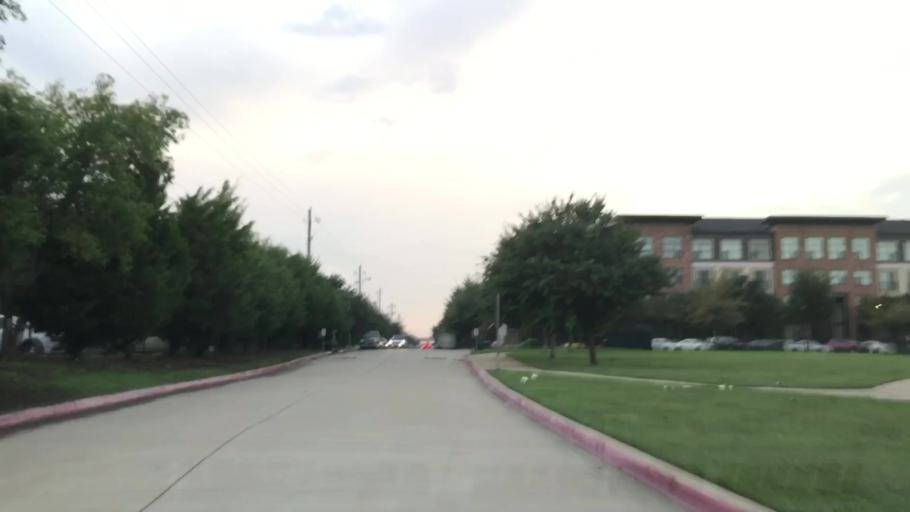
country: US
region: Texas
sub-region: Dallas County
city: Addison
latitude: 33.0110
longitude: -96.8213
